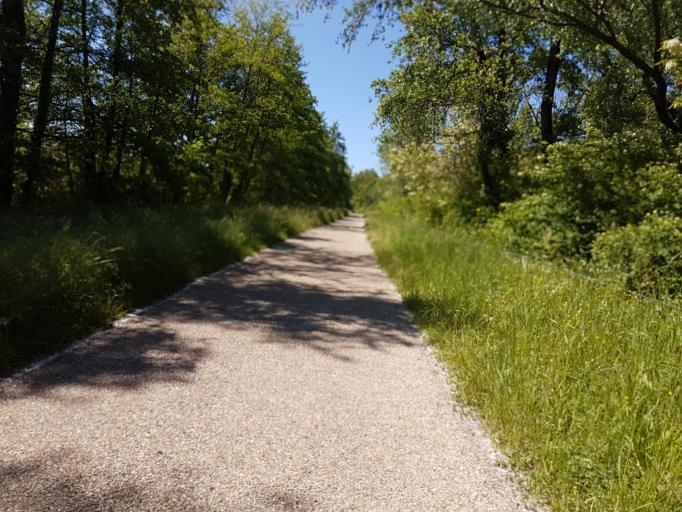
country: FR
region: Rhone-Alpes
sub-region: Departement de la Drome
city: Saint-Vallier
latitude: 45.1457
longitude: 4.8174
